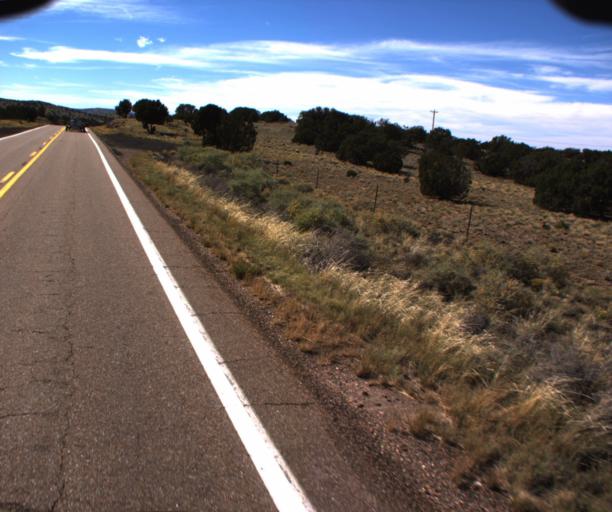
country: US
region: Arizona
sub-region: Apache County
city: Saint Johns
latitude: 34.4834
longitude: -109.5633
